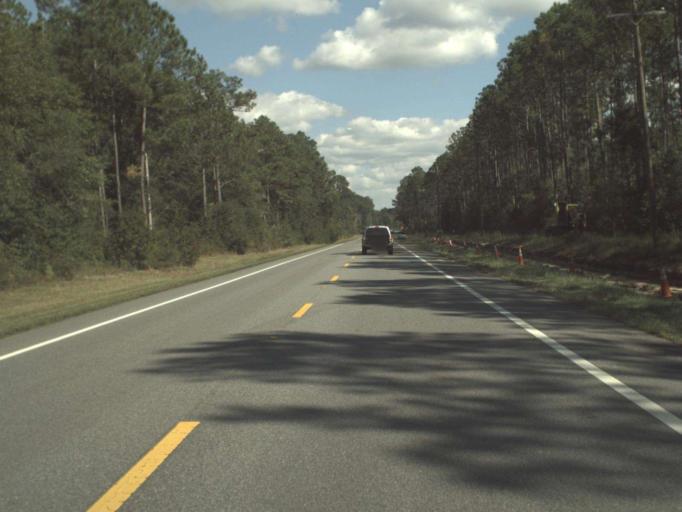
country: US
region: Florida
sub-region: Walton County
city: Freeport
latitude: 30.4734
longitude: -85.9779
